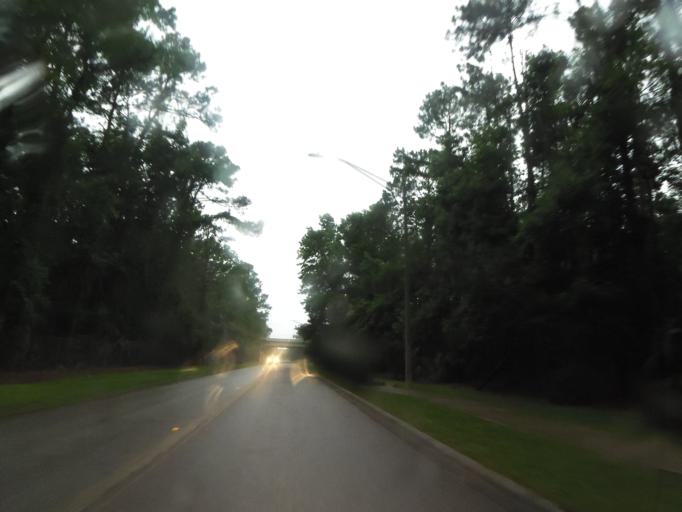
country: US
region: Florida
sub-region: Duval County
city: Neptune Beach
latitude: 30.2811
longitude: -81.5194
